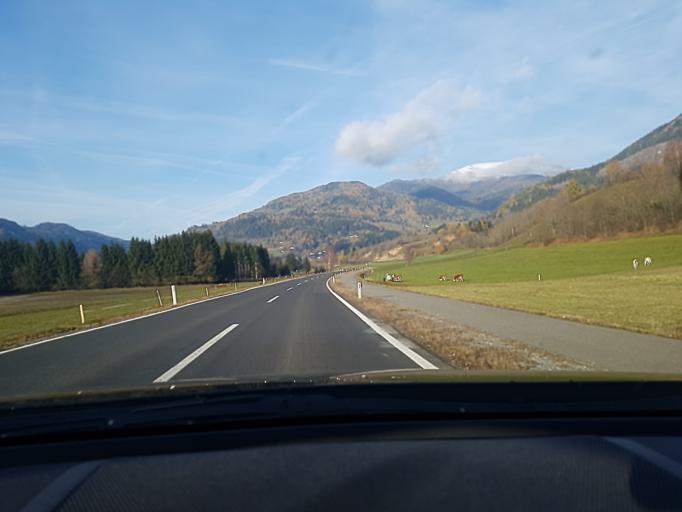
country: AT
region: Styria
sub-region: Politischer Bezirk Murau
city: Sankt Peter am Kammersberg
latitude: 47.1884
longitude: 14.1536
